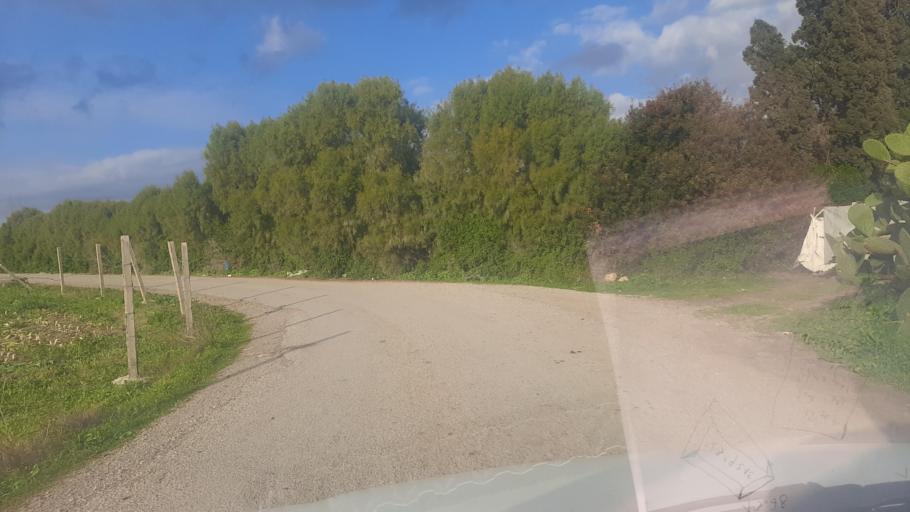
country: TN
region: Nabul
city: Manzil Bu Zalafah
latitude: 36.7099
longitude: 10.5012
